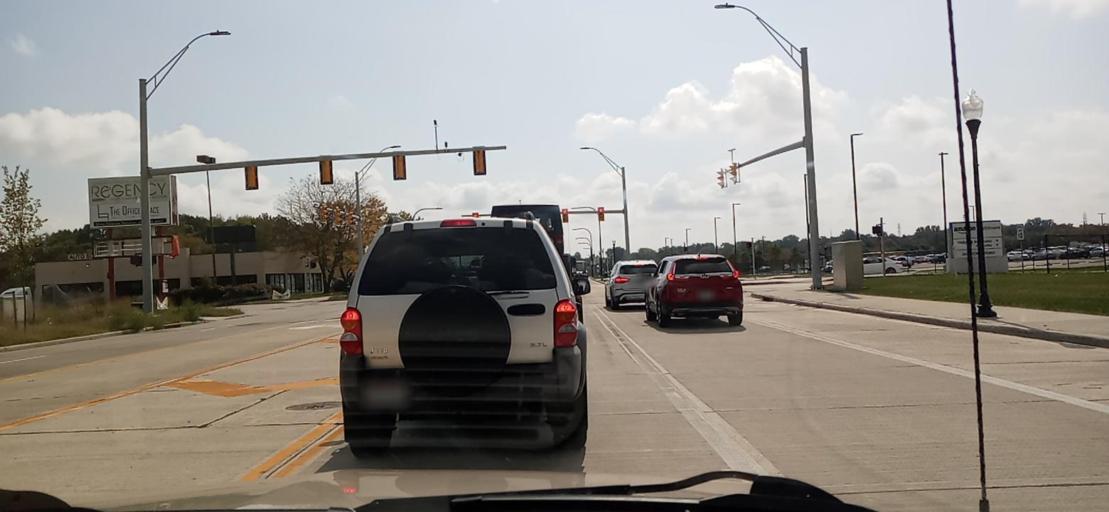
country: US
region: Ohio
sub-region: Summit County
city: Barberton
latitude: 41.0499
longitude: -81.5808
